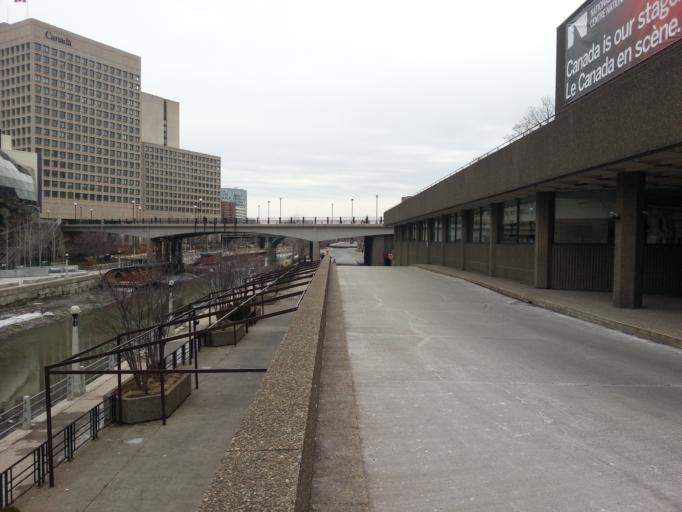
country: CA
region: Ontario
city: Ottawa
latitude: 45.4237
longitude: -75.6929
